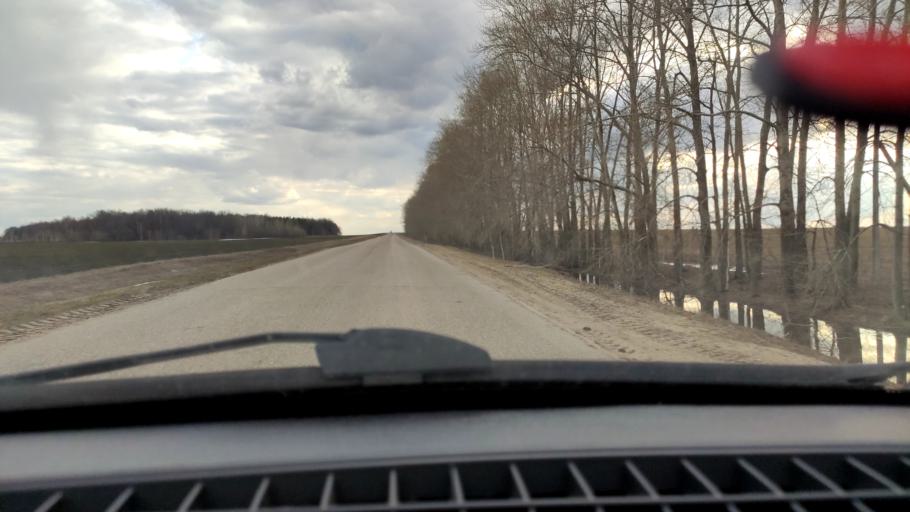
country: RU
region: Bashkortostan
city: Karmaskaly
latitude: 54.3048
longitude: 55.9341
